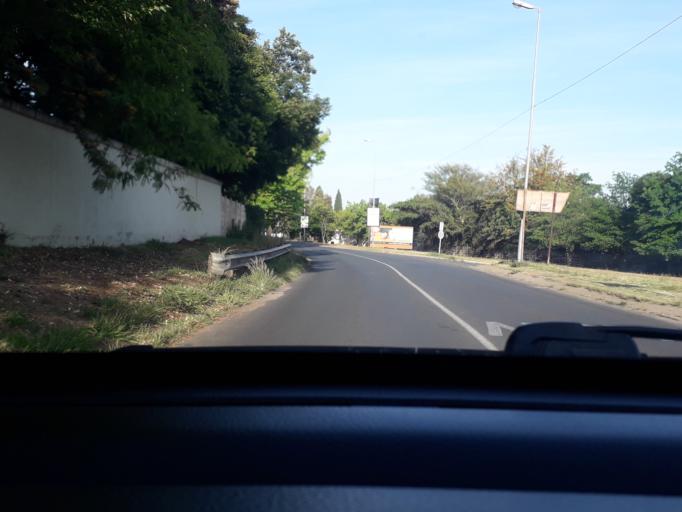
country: ZA
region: Gauteng
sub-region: City of Johannesburg Metropolitan Municipality
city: Modderfontein
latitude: -26.0657
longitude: 28.0796
